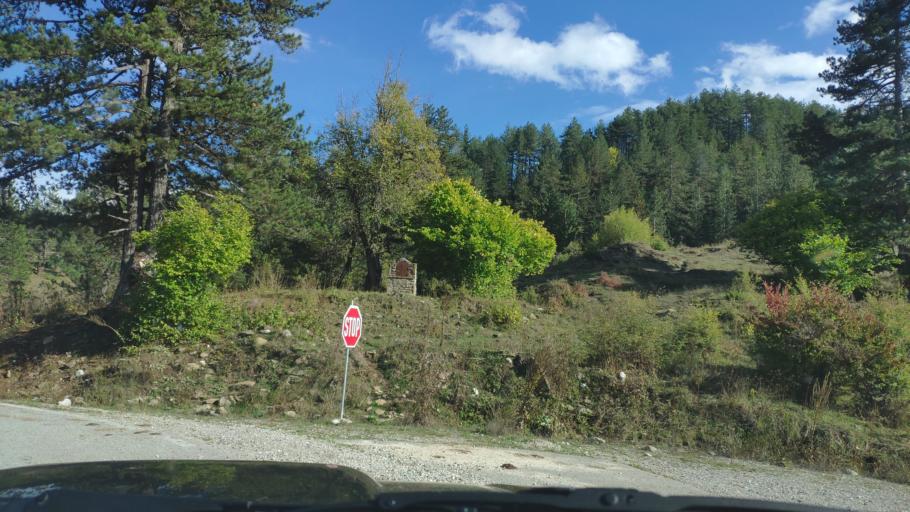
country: AL
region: Korce
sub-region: Rrethi i Devollit
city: Miras
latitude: 40.3979
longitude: 20.8822
